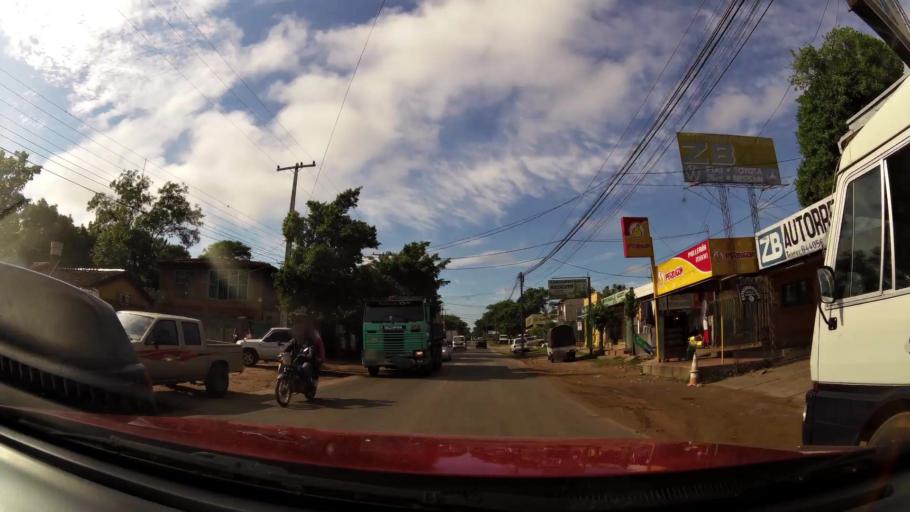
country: PY
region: Central
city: San Lorenzo
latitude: -25.2737
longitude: -57.4866
